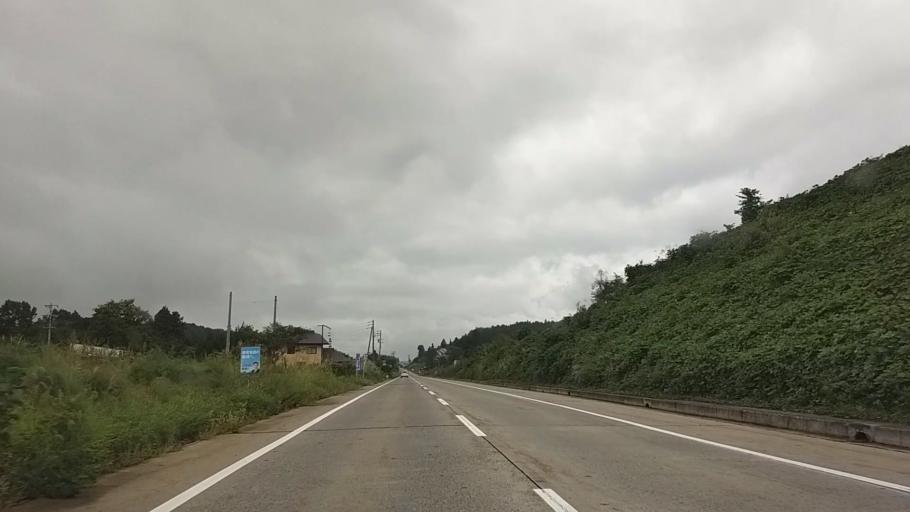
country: JP
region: Nagano
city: Iiyama
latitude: 36.8096
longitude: 138.3351
